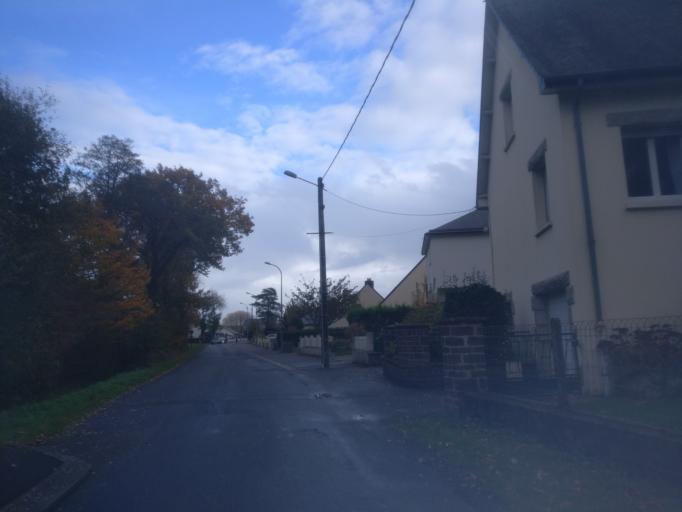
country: FR
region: Brittany
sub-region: Departement d'Ille-et-Vilaine
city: Guichen
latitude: 47.9995
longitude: -1.7817
